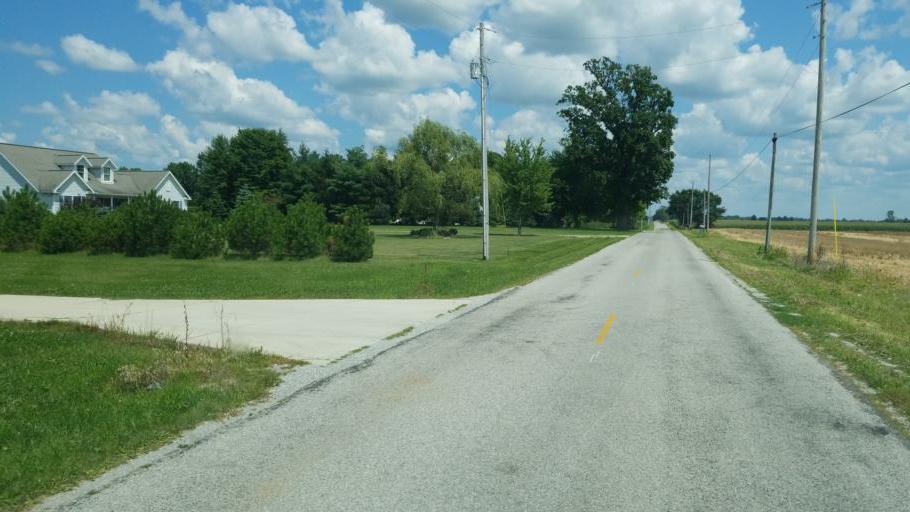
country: US
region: Ohio
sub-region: Marion County
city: Marion
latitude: 40.6376
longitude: -83.0173
